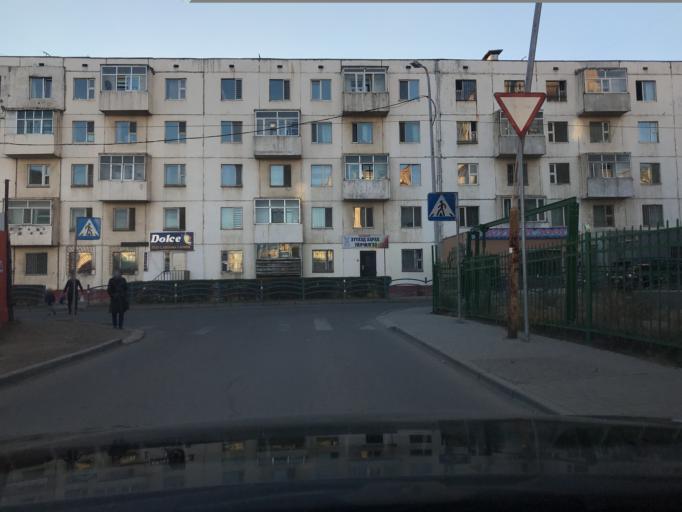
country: MN
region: Ulaanbaatar
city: Ulaanbaatar
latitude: 47.9256
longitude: 106.9063
